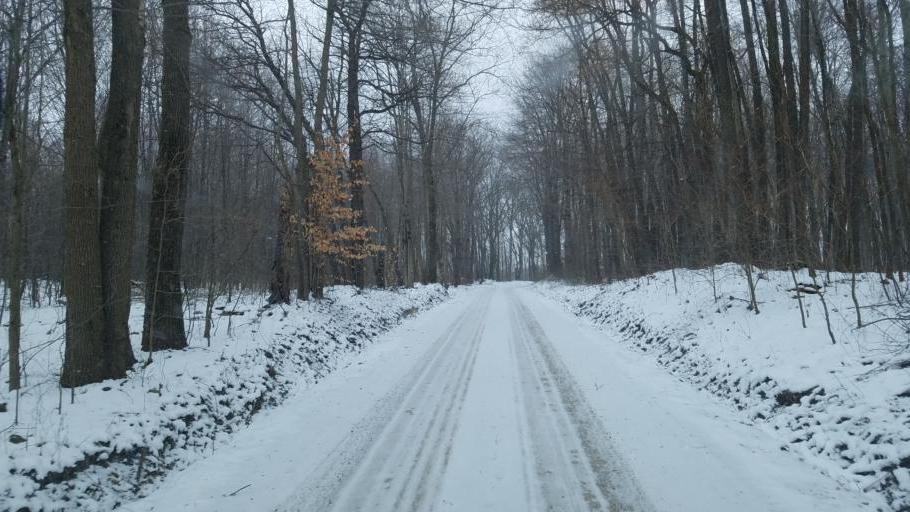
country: US
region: Pennsylvania
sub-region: Crawford County
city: Cochranton
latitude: 41.4461
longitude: -79.9921
